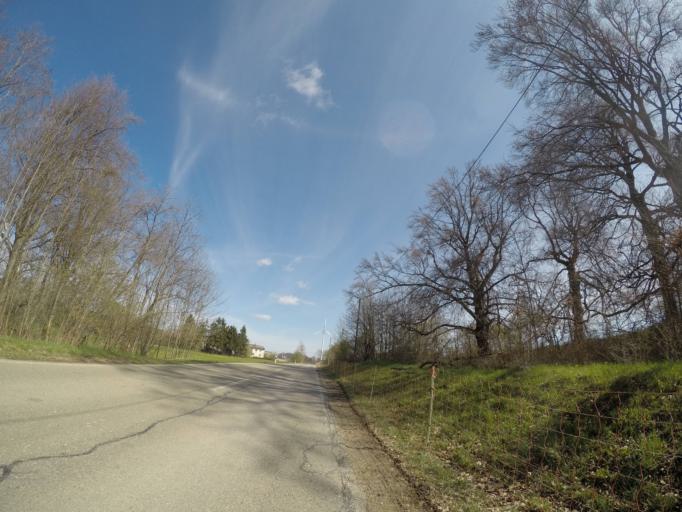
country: DE
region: Baden-Wuerttemberg
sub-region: Regierungsbezirk Stuttgart
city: Wiesensteig
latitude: 48.5471
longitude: 9.6261
